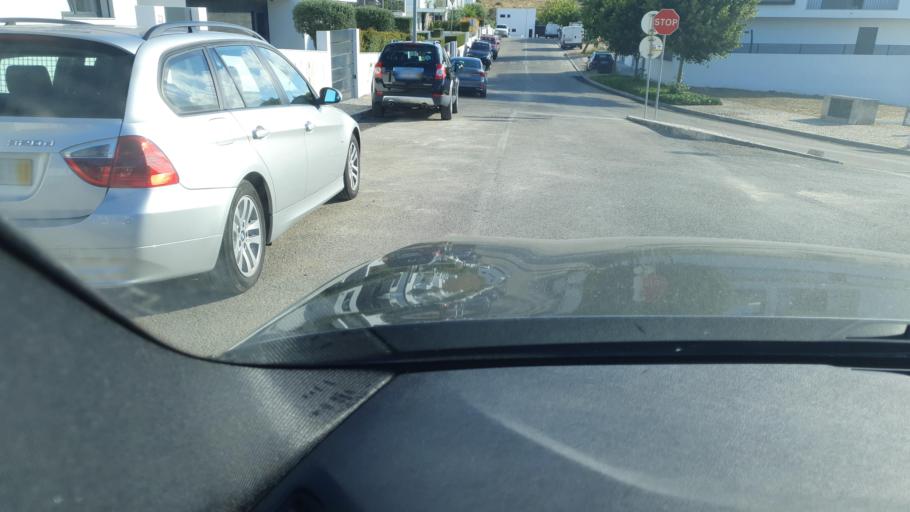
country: PT
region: Lisbon
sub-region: Sintra
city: Belas
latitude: 38.8050
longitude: -9.2544
